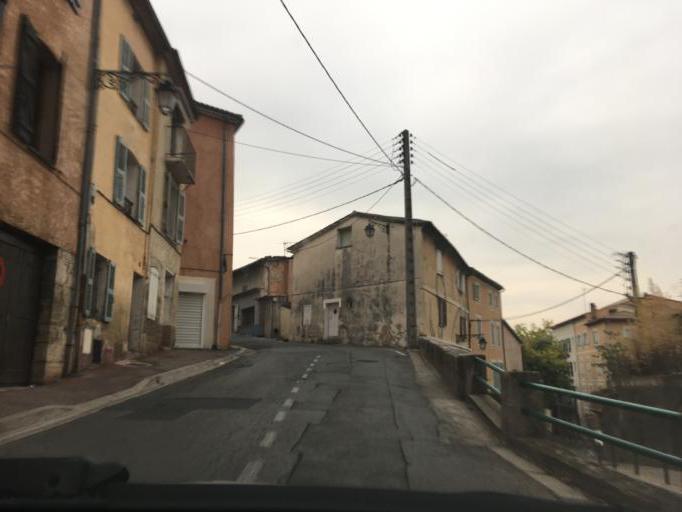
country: FR
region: Provence-Alpes-Cote d'Azur
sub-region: Departement du Var
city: Draguignan
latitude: 43.5411
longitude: 6.4666
